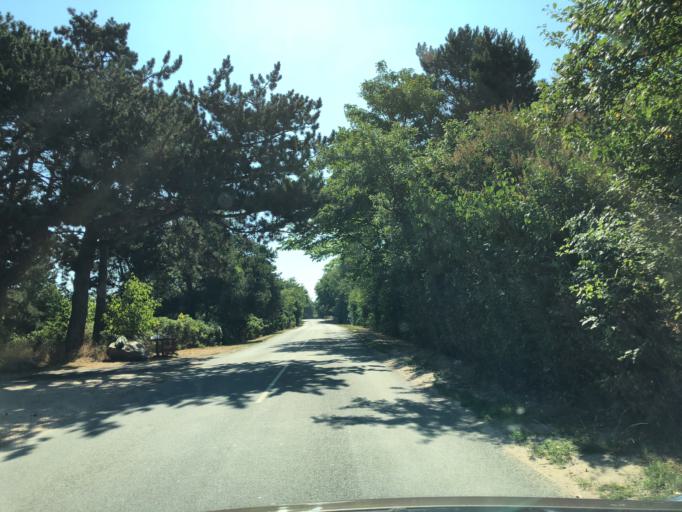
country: DK
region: Zealand
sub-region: Odsherred Kommune
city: Asnaes
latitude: 55.9830
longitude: 11.3075
